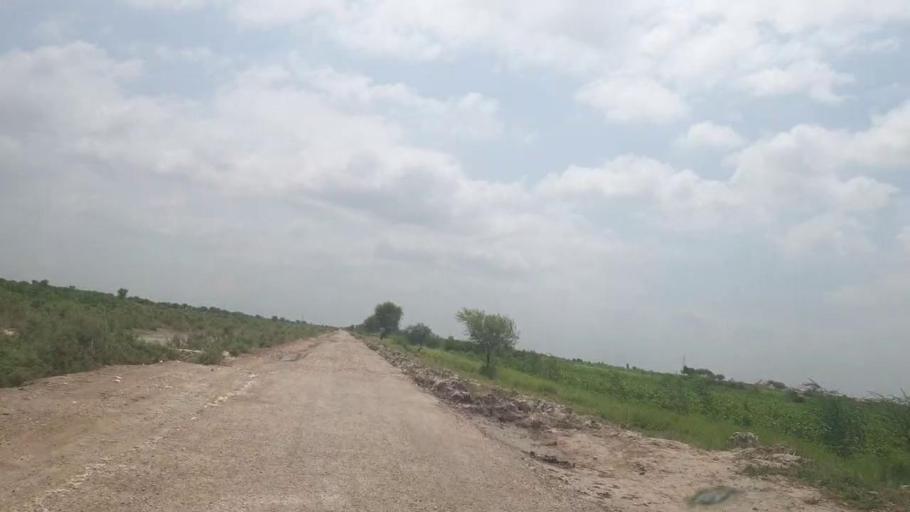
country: PK
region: Sindh
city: Tando Mittha Khan
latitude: 25.8870
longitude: 69.1612
